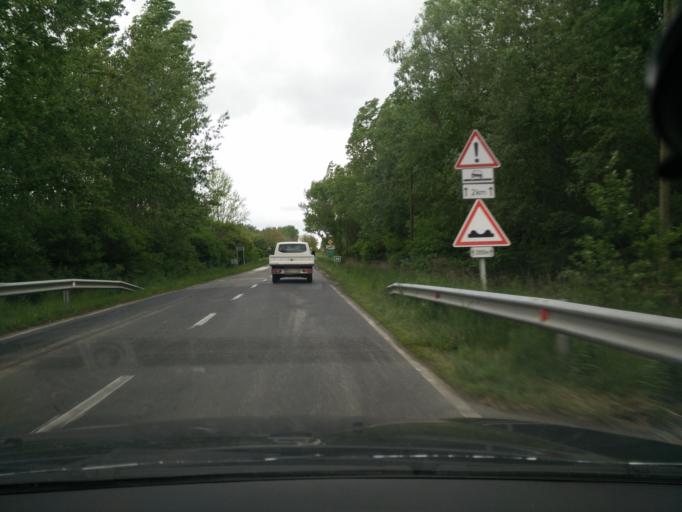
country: HU
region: Veszprem
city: Papa
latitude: 47.4045
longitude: 17.4690
